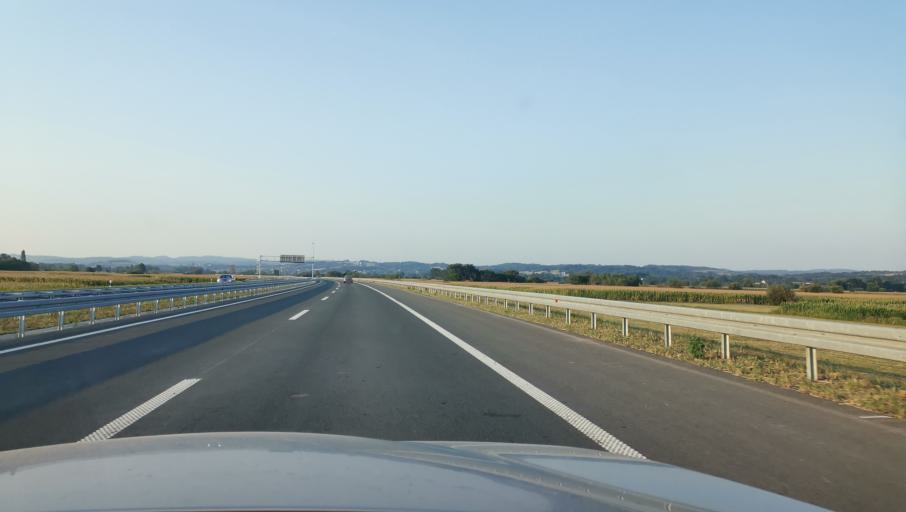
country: RS
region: Central Serbia
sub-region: Kolubarski Okrug
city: Ljig
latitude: 44.2469
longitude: 20.2671
